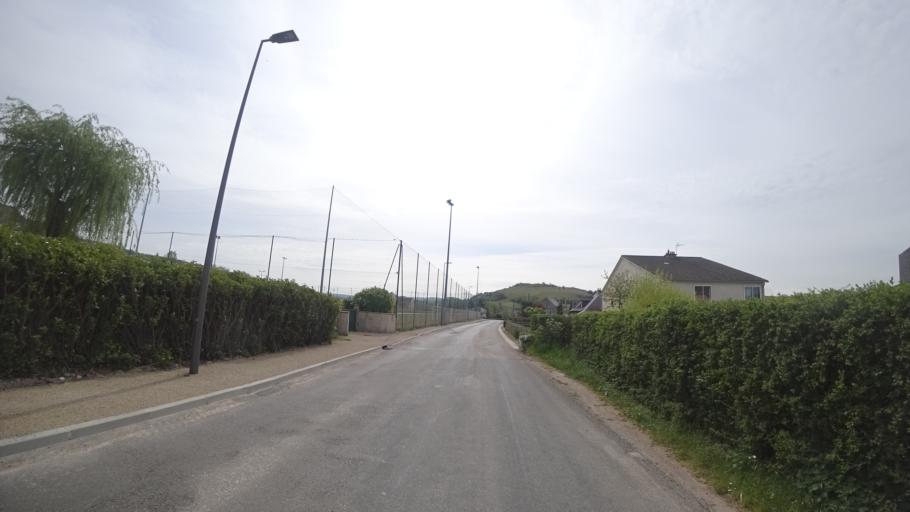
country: FR
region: Midi-Pyrenees
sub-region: Departement de l'Aveyron
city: Sebazac-Concoures
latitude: 44.3778
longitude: 2.6053
